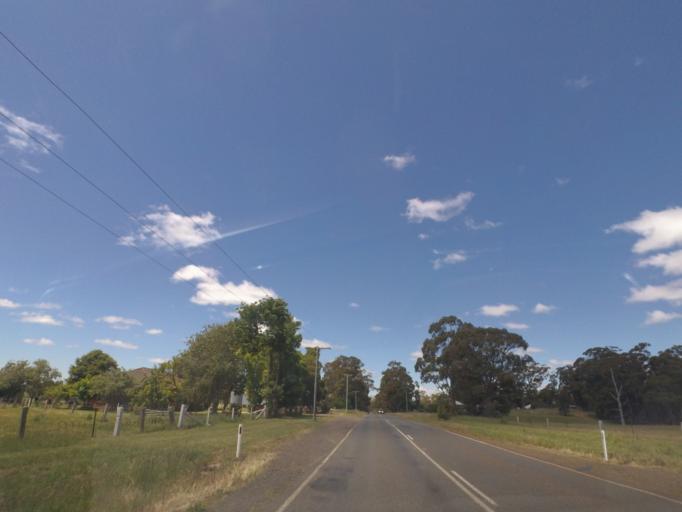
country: AU
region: Victoria
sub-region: Mount Alexander
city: Castlemaine
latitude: -37.3194
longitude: 144.2084
